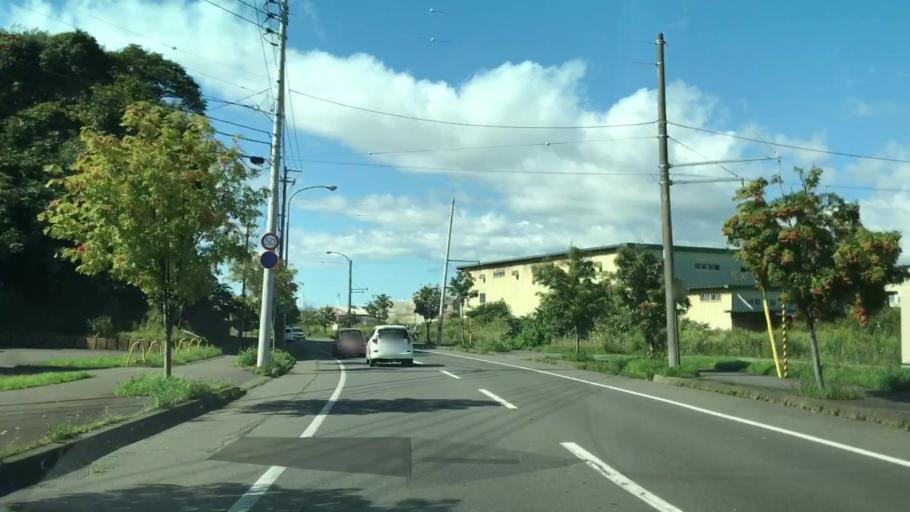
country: JP
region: Hokkaido
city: Muroran
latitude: 42.3288
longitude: 140.9675
